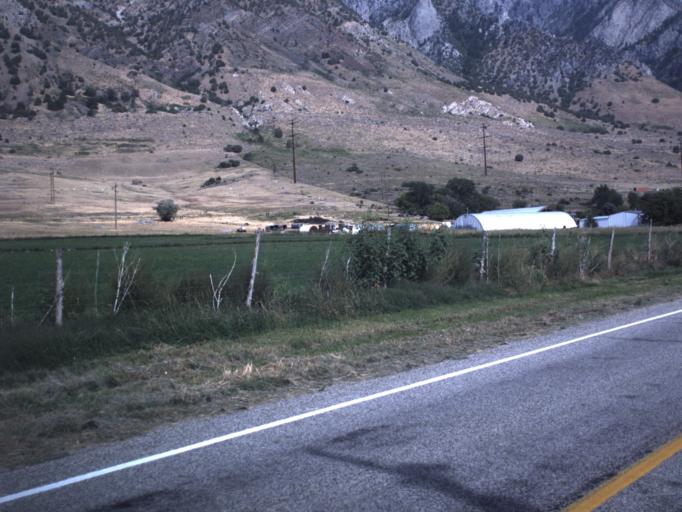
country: US
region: Utah
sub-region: Box Elder County
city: Honeyville
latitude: 41.6008
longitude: -112.0508
